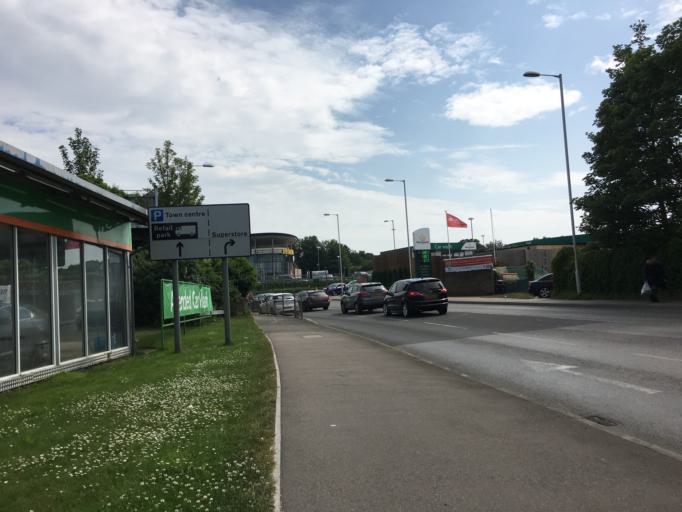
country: GB
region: England
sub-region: Kent
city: Sittingbourne
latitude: 51.3450
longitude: 0.7323
